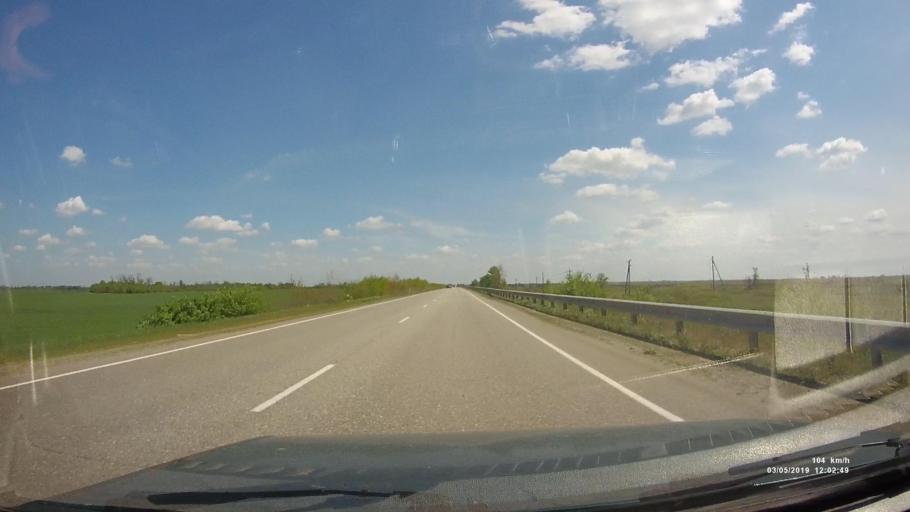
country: RU
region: Rostov
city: Bagayevskaya
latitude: 47.2726
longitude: 40.3763
